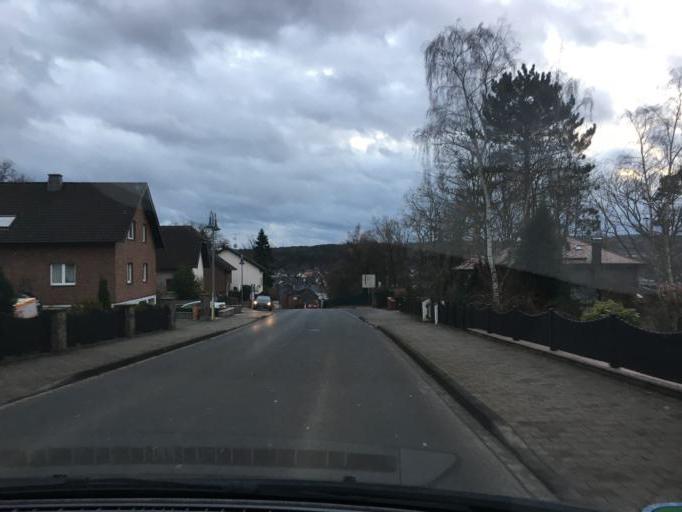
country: DE
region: North Rhine-Westphalia
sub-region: Regierungsbezirk Koln
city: Mechernich
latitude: 50.5962
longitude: 6.6531
